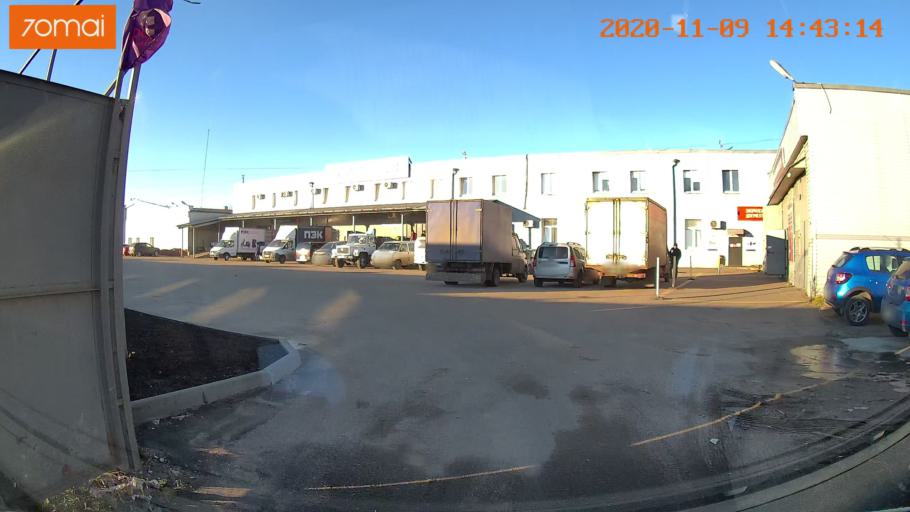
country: RU
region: Ivanovo
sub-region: Gorod Ivanovo
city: Ivanovo
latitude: 56.9989
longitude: 40.9163
